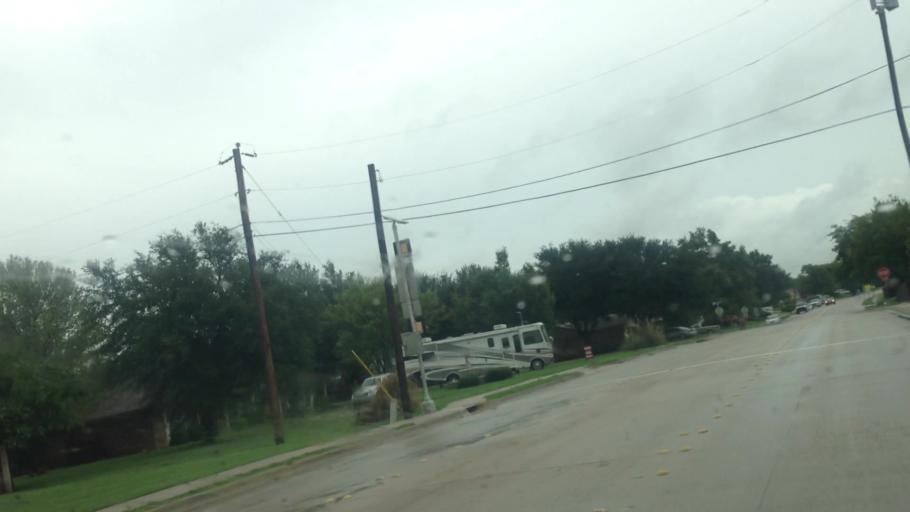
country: US
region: Texas
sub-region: Tarrant County
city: Watauga
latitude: 32.8824
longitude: -97.2497
